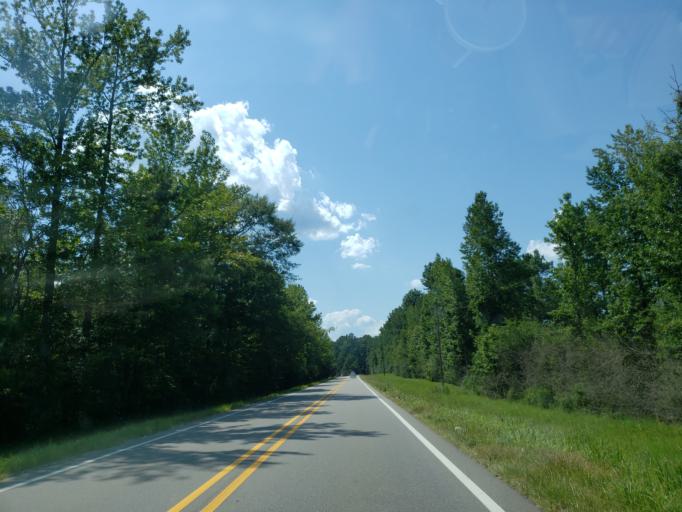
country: US
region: Mississippi
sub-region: Lamar County
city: Sumrall
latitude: 31.3779
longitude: -89.5141
